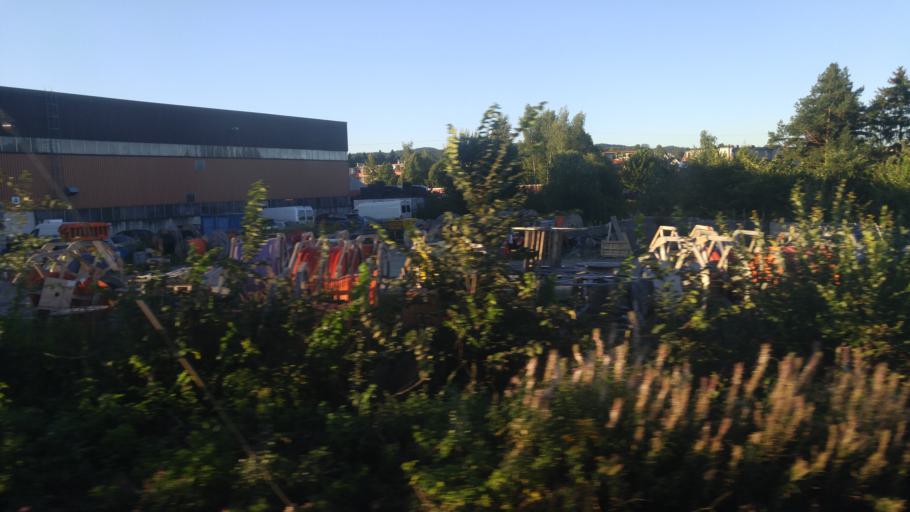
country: NO
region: Akershus
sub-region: Lorenskog
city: Kjenn
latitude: 59.9538
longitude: 10.8963
